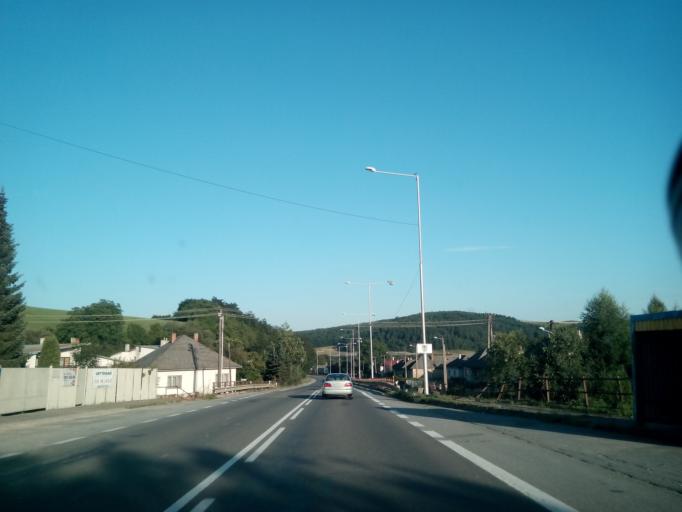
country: SK
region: Presovsky
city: Sabinov
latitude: 49.0068
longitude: 21.0694
